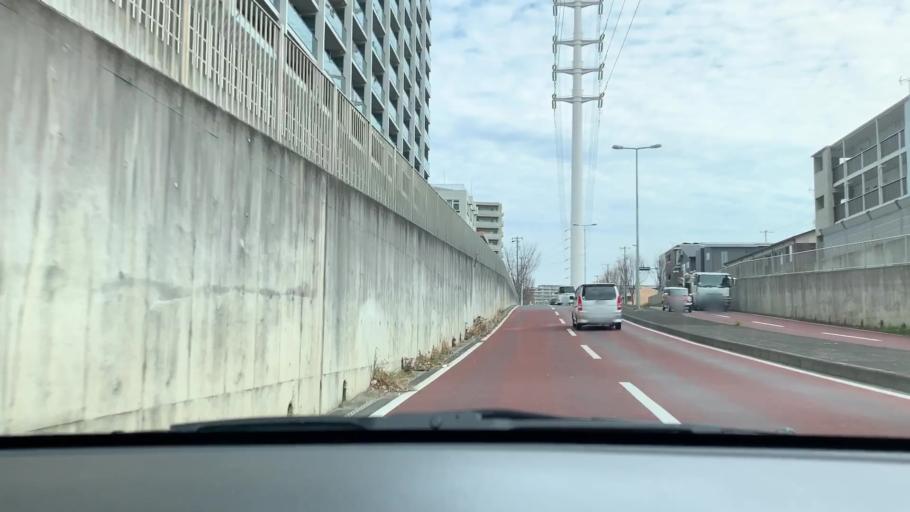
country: JP
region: Chiba
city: Nagareyama
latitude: 35.8713
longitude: 139.9285
